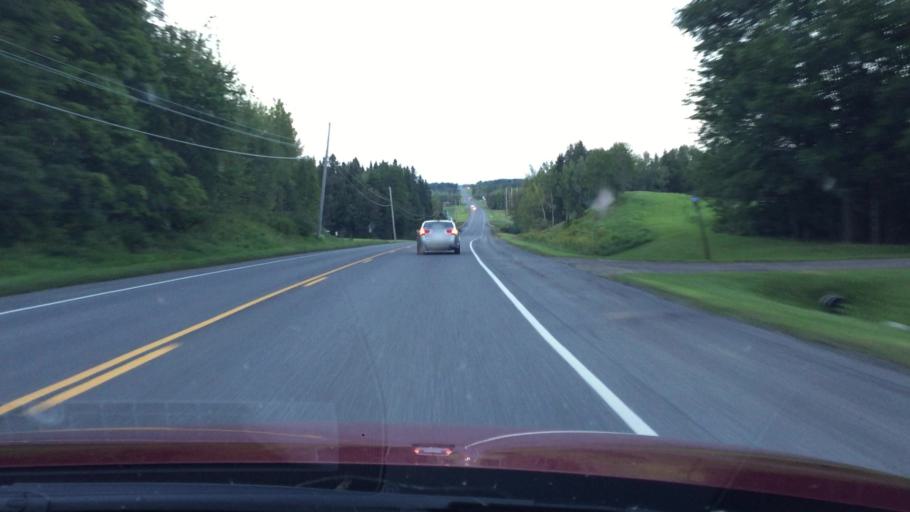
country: US
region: Maine
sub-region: Aroostook County
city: Easton
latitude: 46.4697
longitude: -67.8686
